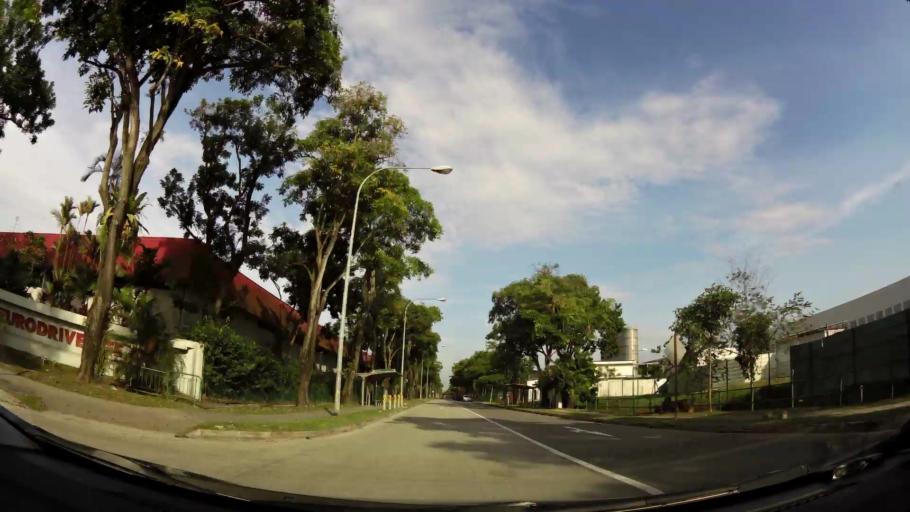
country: MY
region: Johor
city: Johor Bahru
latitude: 1.3251
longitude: 103.6573
